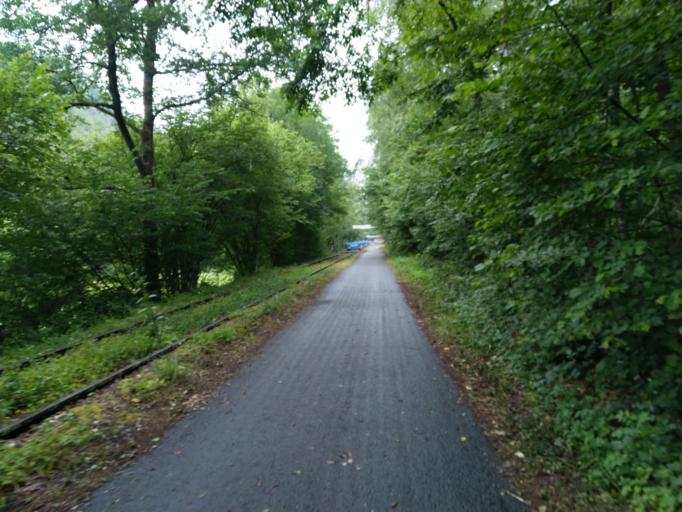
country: BE
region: Wallonia
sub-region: Province de Namur
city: Anhee
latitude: 50.3119
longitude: 4.8328
